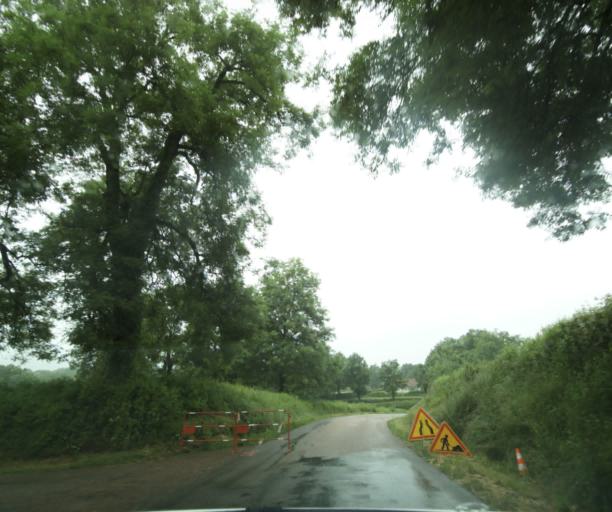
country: FR
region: Bourgogne
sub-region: Departement de Saone-et-Loire
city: Charolles
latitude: 46.4117
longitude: 4.2046
